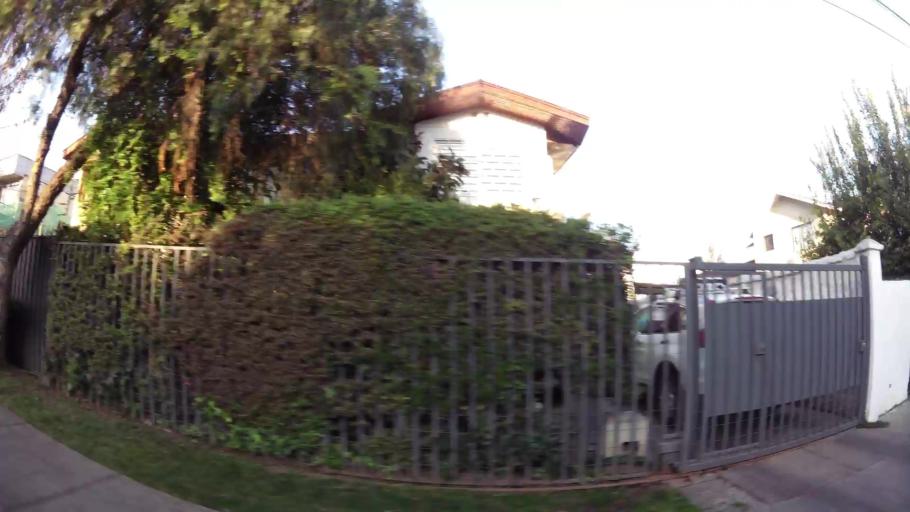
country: CL
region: Santiago Metropolitan
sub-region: Provincia de Santiago
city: Villa Presidente Frei, Nunoa, Santiago, Chile
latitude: -33.4000
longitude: -70.5578
